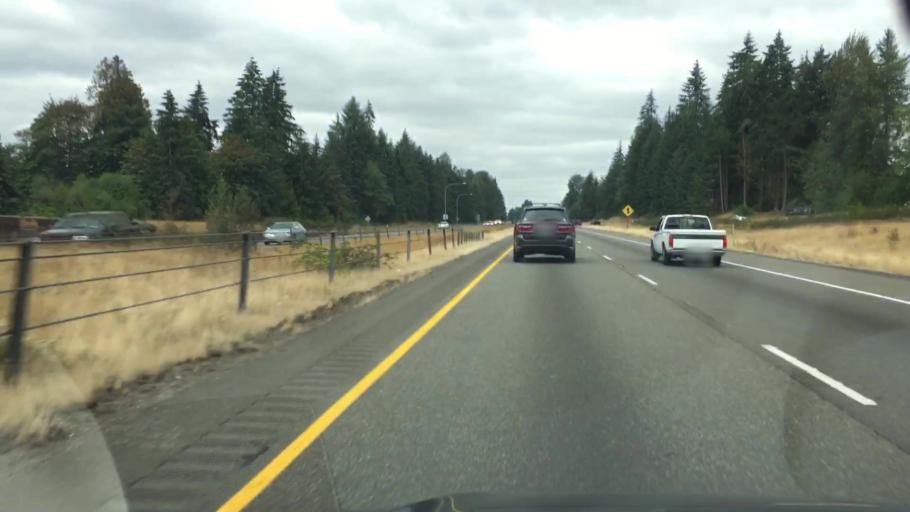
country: US
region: Washington
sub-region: Pierce County
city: Summit
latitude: 47.1582
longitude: -122.3579
